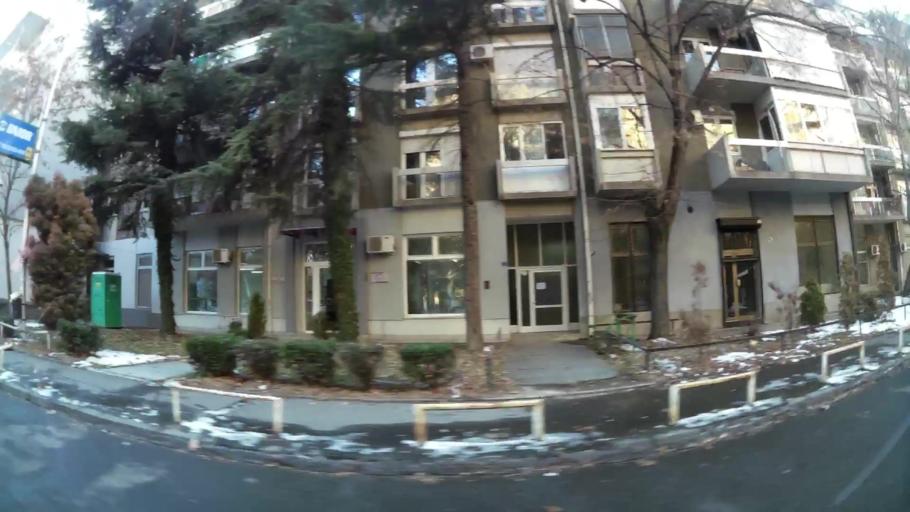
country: MK
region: Karpos
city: Skopje
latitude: 41.9941
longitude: 21.4112
